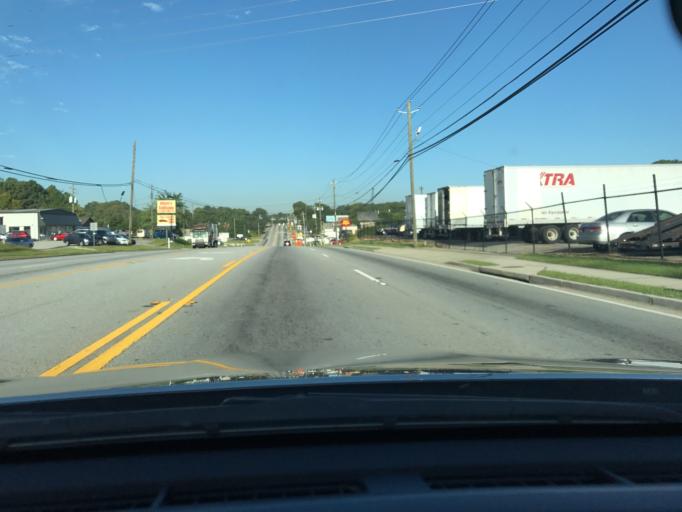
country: US
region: Georgia
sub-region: Clayton County
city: Lake City
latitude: 33.6106
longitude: -84.3314
